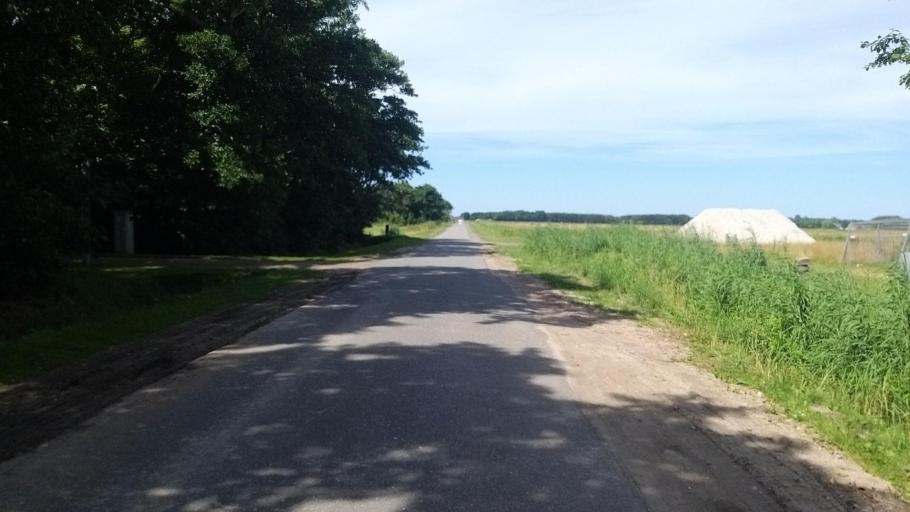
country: NL
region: North Holland
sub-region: Gemeente Texel
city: Den Burg
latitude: 53.1419
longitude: 4.8731
